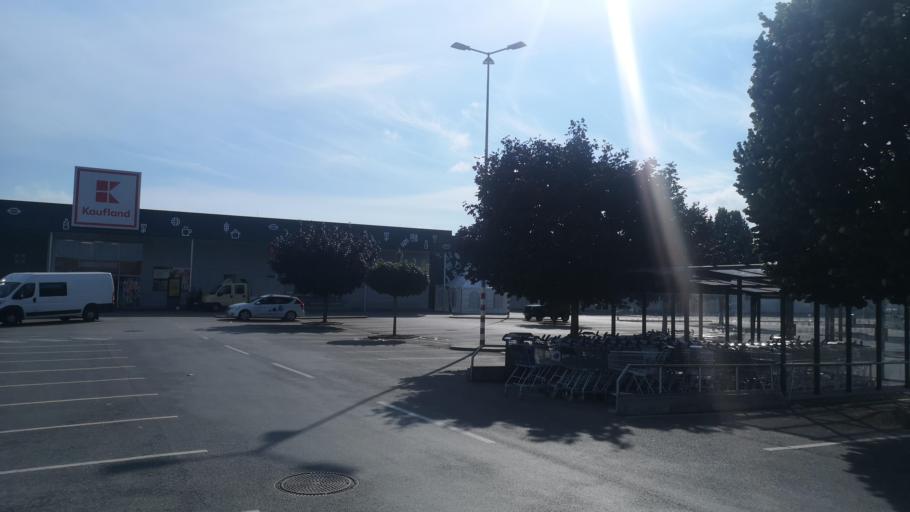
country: SK
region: Trnavsky
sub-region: Okres Trnava
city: Trnava
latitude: 48.3832
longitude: 17.6003
